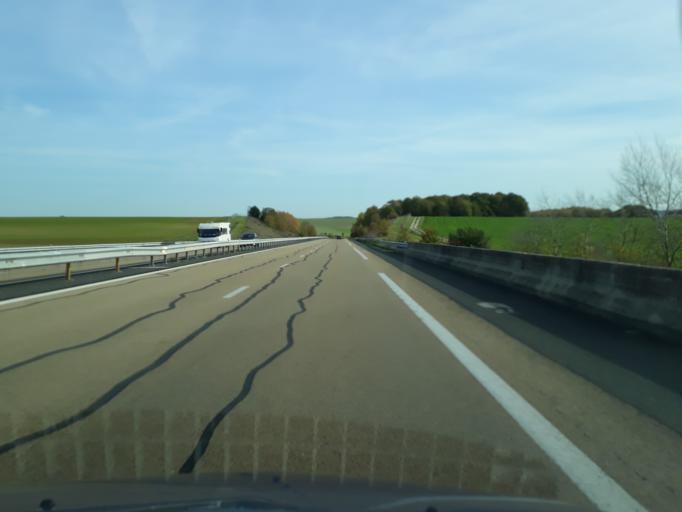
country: FR
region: Champagne-Ardenne
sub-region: Departement de l'Aube
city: Aix-en-Othe
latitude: 48.2688
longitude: 3.7025
